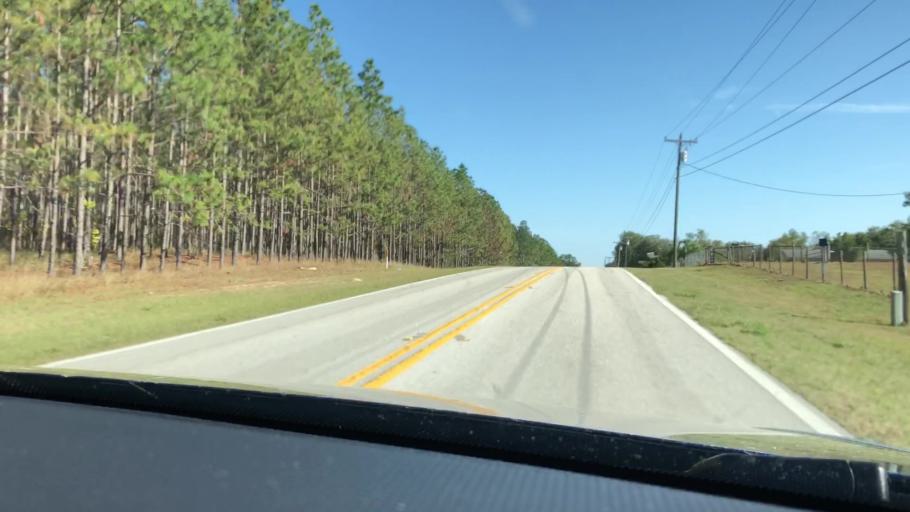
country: US
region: Florida
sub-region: Lake County
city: Eustis
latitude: 28.8733
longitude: -81.6155
